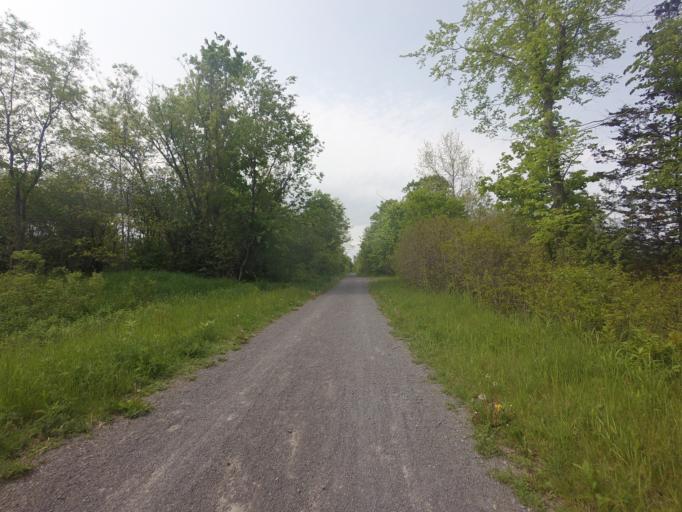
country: CA
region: Ontario
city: Kingston
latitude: 44.3216
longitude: -76.5873
